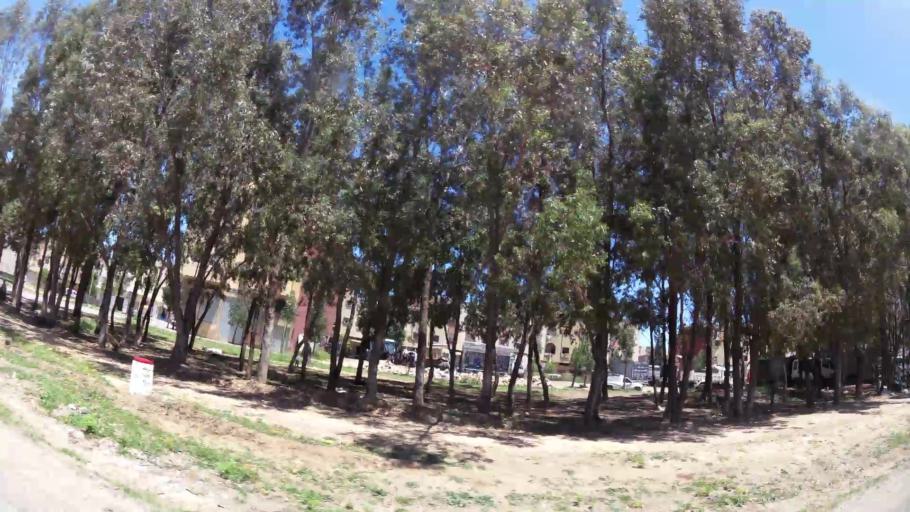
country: MA
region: Meknes-Tafilalet
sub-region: Meknes
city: Meknes
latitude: 33.8494
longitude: -5.5583
